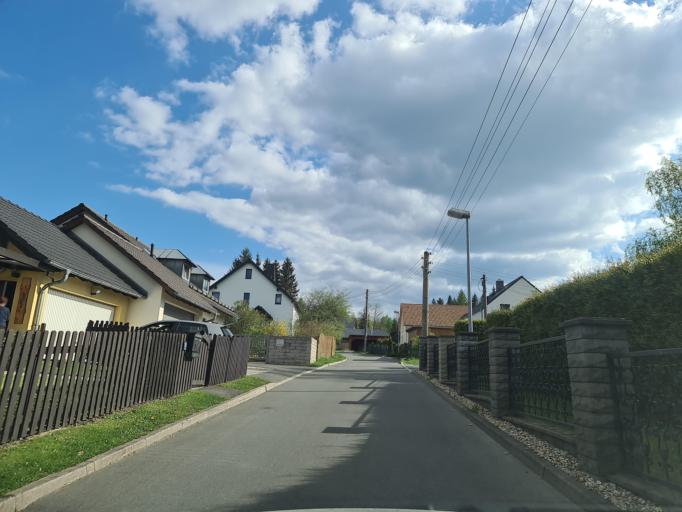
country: DE
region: Saxony
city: Ellefeld
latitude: 50.4680
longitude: 12.3906
